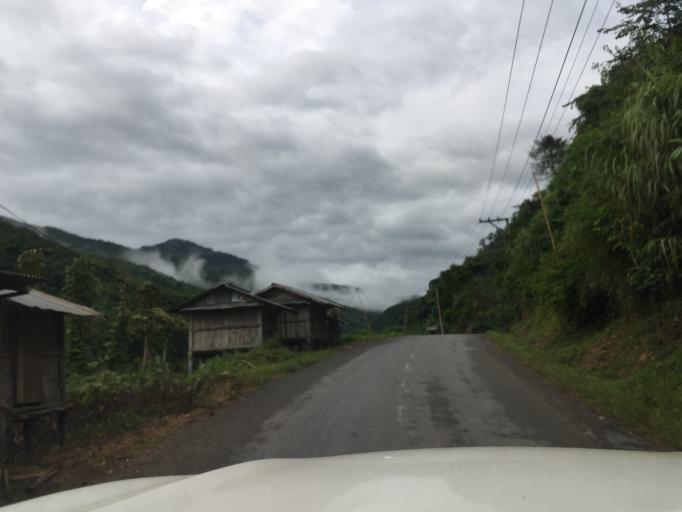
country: LA
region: Oudomxai
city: Muang La
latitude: 21.0517
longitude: 102.2412
